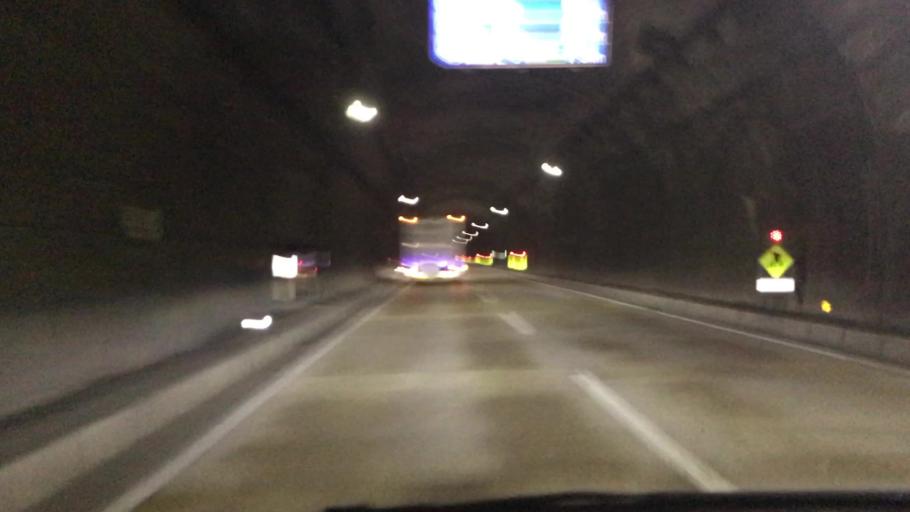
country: JP
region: Hyogo
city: Kobe
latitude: 34.7580
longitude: 135.1607
